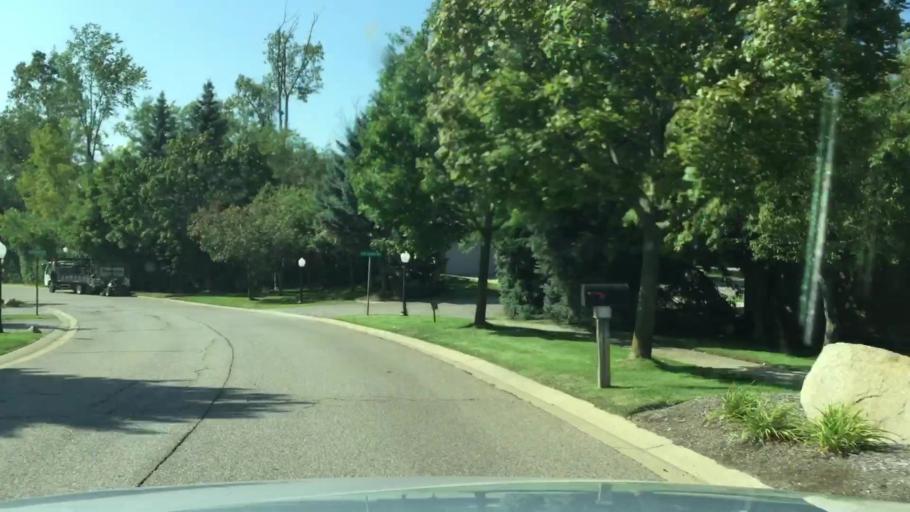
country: US
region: Michigan
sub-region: Oakland County
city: Walled Lake
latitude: 42.5253
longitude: -83.4572
